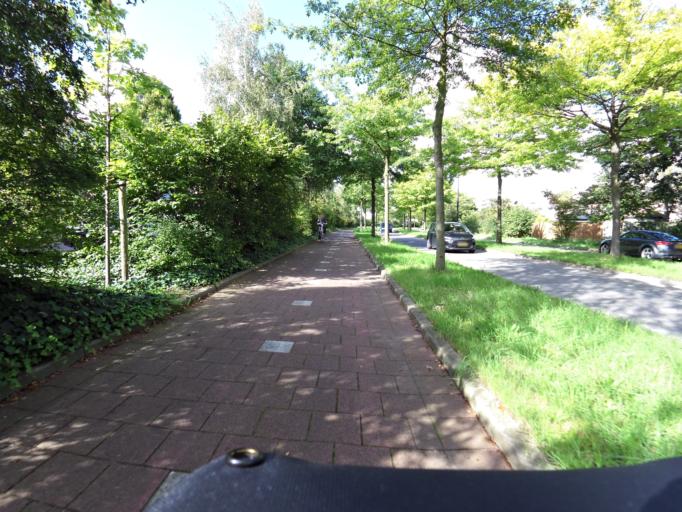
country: NL
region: South Holland
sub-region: Gemeente Vlaardingen
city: Vlaardingen
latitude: 51.9355
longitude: 4.3347
